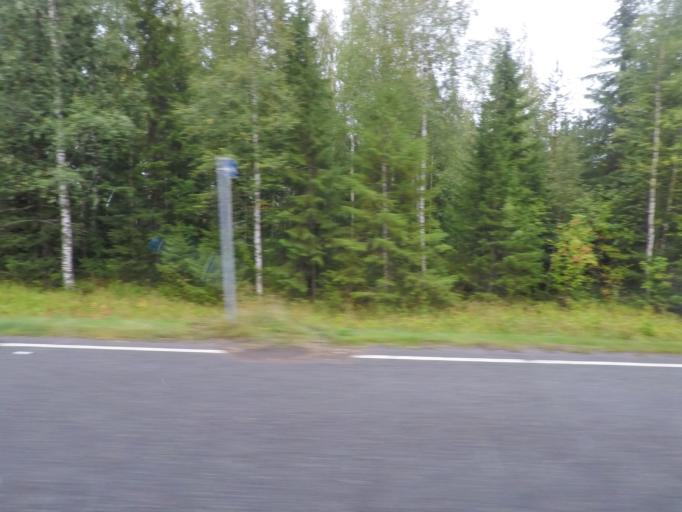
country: FI
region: Southern Savonia
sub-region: Pieksaemaeki
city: Juva
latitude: 62.0352
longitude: 27.7995
